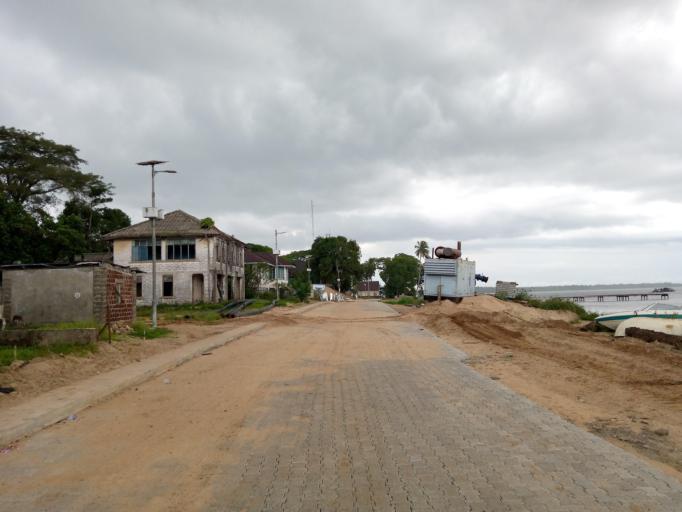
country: SL
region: Southern Province
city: Bonthe
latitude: 7.5313
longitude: -12.5017
